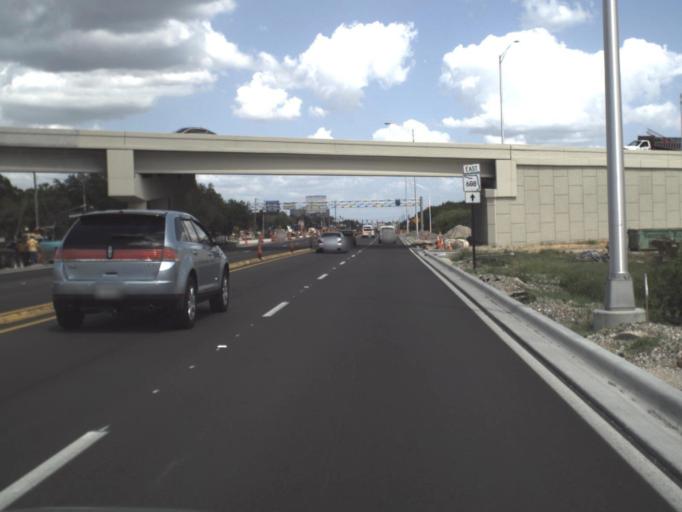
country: US
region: Florida
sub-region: Pinellas County
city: Feather Sound
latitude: 27.8937
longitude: -82.6746
